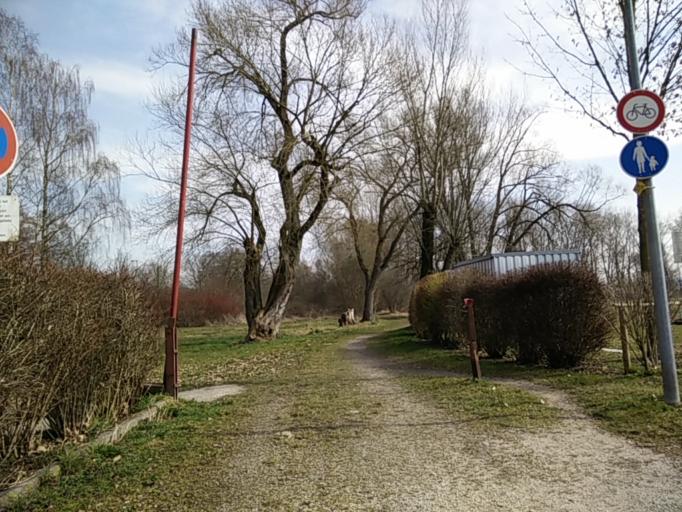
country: DE
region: Baden-Wuerttemberg
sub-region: Freiburg Region
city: Radolfzell am Bodensee
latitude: 47.7386
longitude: 9.0034
